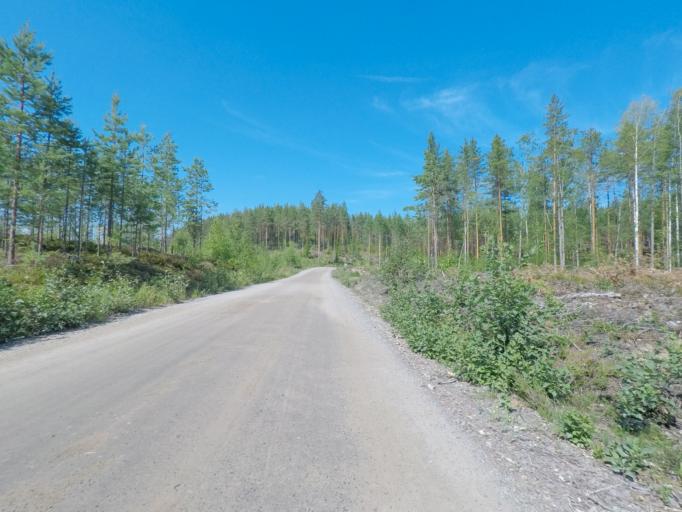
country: FI
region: Southern Savonia
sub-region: Mikkeli
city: Puumala
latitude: 61.4056
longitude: 28.0476
